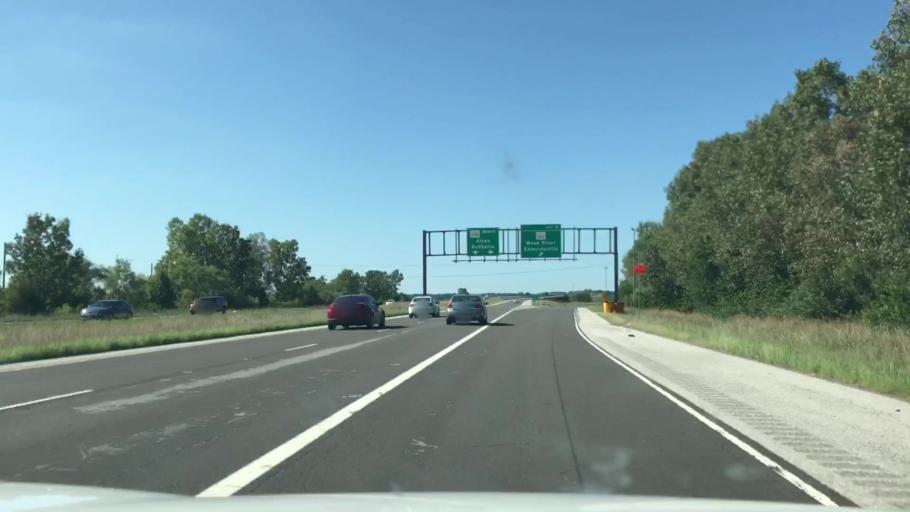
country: US
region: Illinois
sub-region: Madison County
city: South Roxana
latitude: 38.8459
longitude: -90.0480
